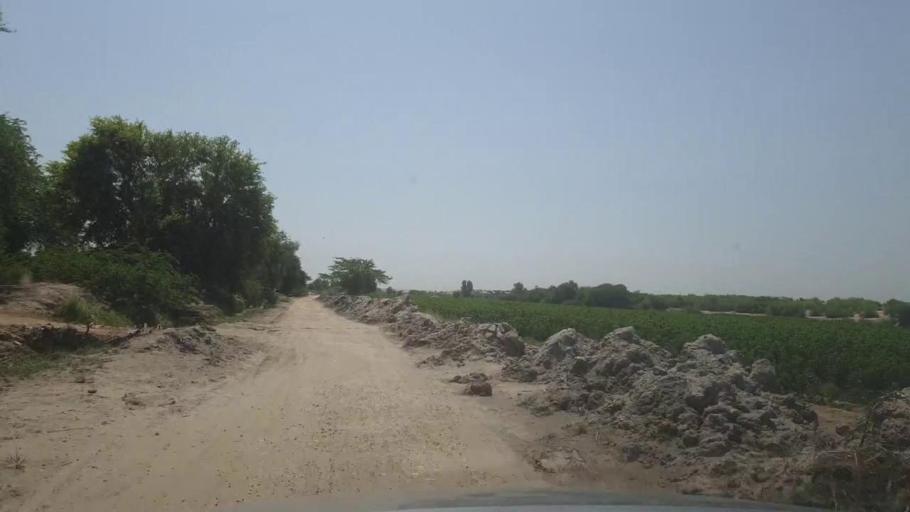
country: PK
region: Sindh
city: Khairpur
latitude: 27.3535
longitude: 69.0434
